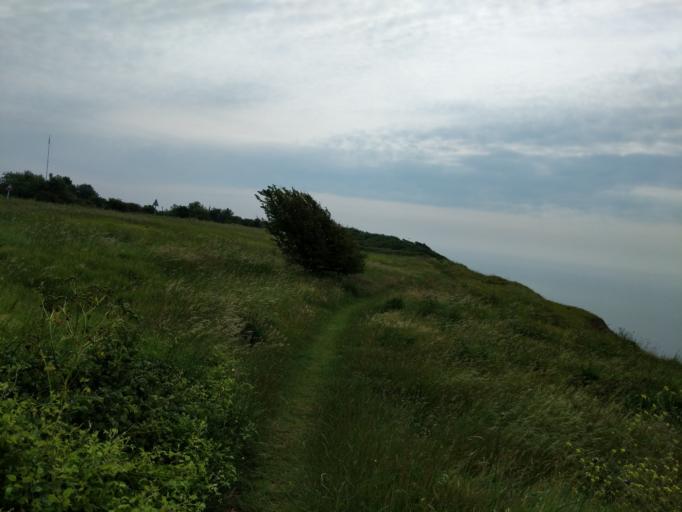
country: GB
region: England
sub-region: Kent
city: Folkestone
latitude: 51.1017
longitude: 1.2229
